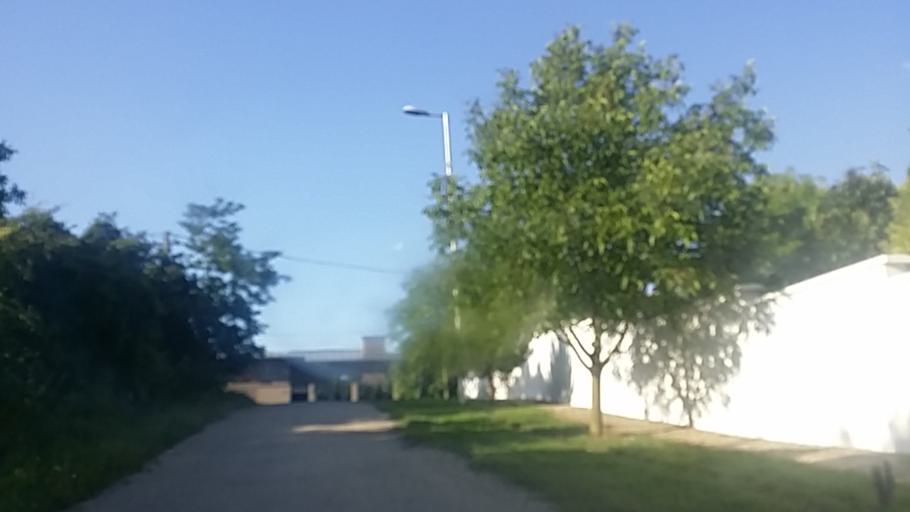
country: HU
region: Pest
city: Urom
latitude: 47.5766
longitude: 19.0236
